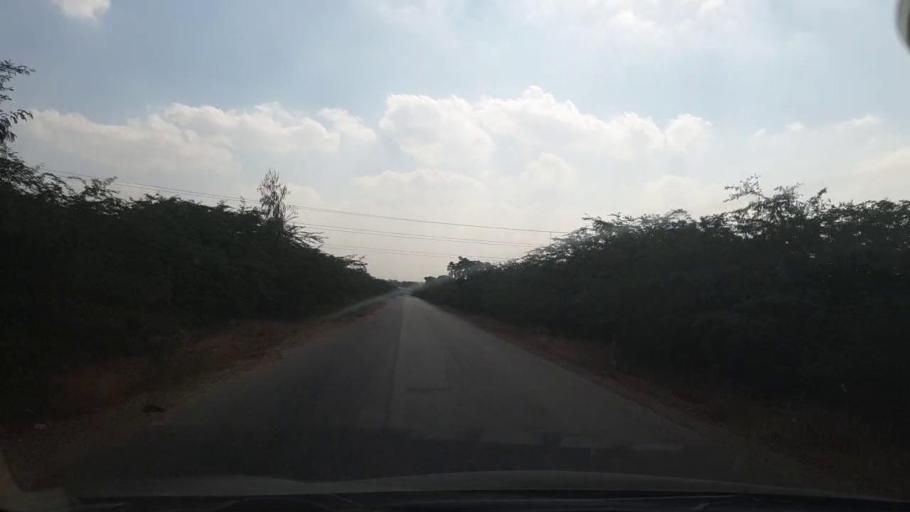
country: PK
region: Sindh
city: Malir Cantonment
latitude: 25.0114
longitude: 67.3540
